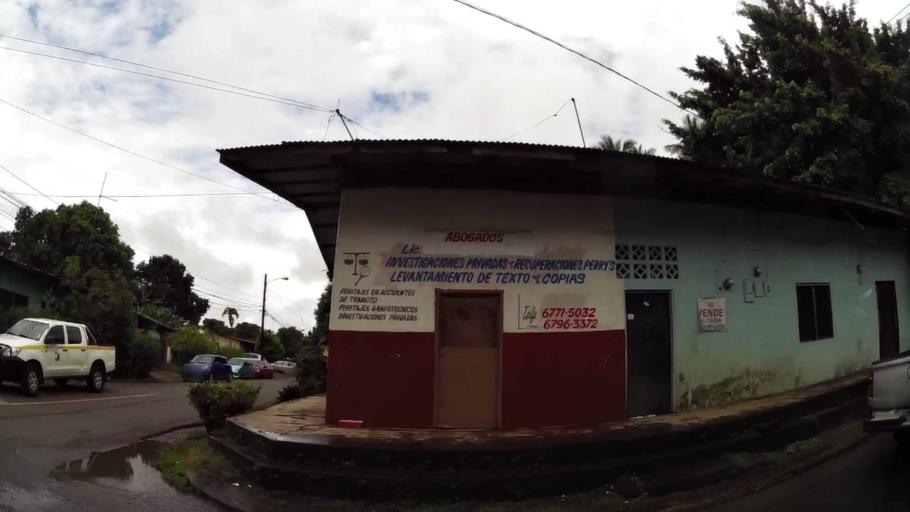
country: PA
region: Chiriqui
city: David
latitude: 8.4239
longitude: -82.4285
